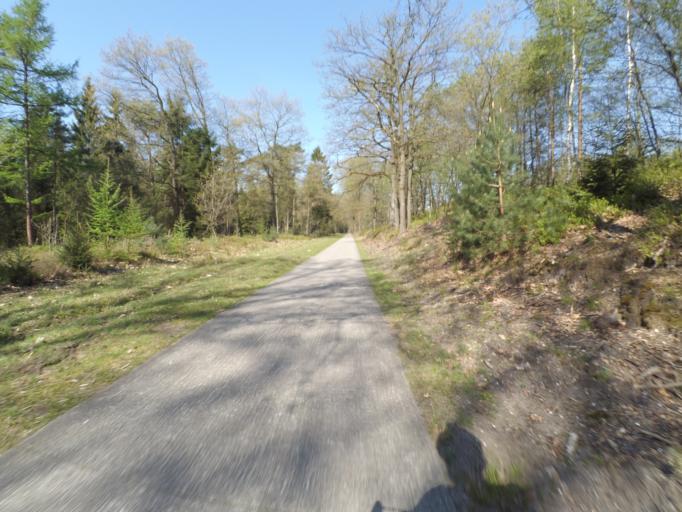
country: NL
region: Gelderland
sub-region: Gemeente Apeldoorn
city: Beekbergen
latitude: 52.1920
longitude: 5.8876
